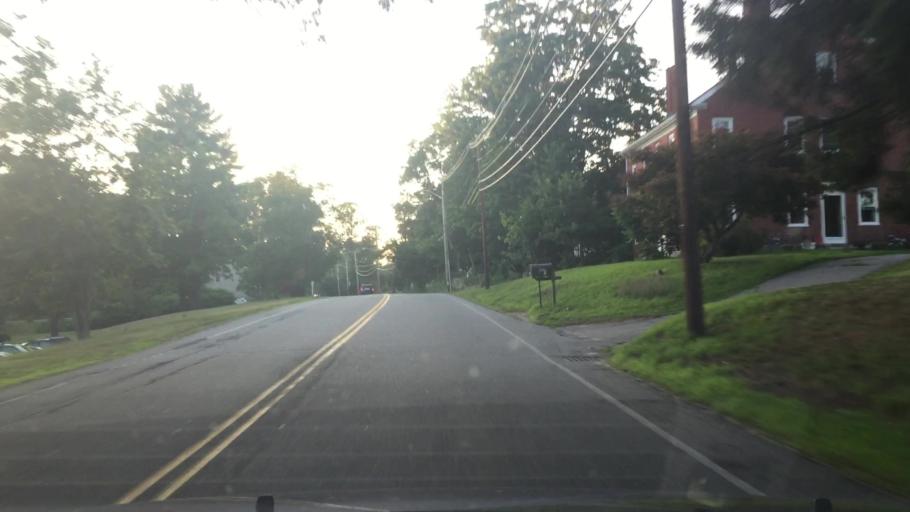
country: US
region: New Hampshire
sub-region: Rockingham County
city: Plaistow
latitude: 42.8098
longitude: -71.0884
